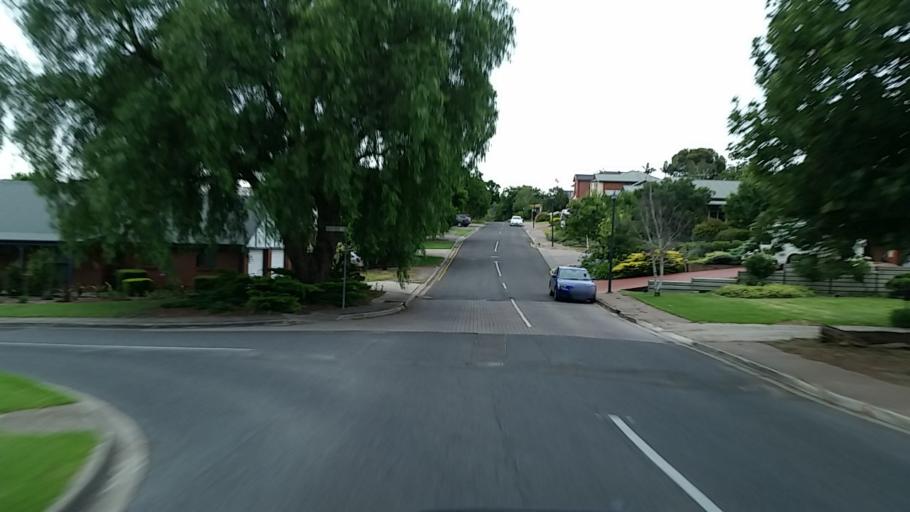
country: AU
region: South Australia
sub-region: Campbelltown
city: Athelstone
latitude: -34.8666
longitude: 138.6935
